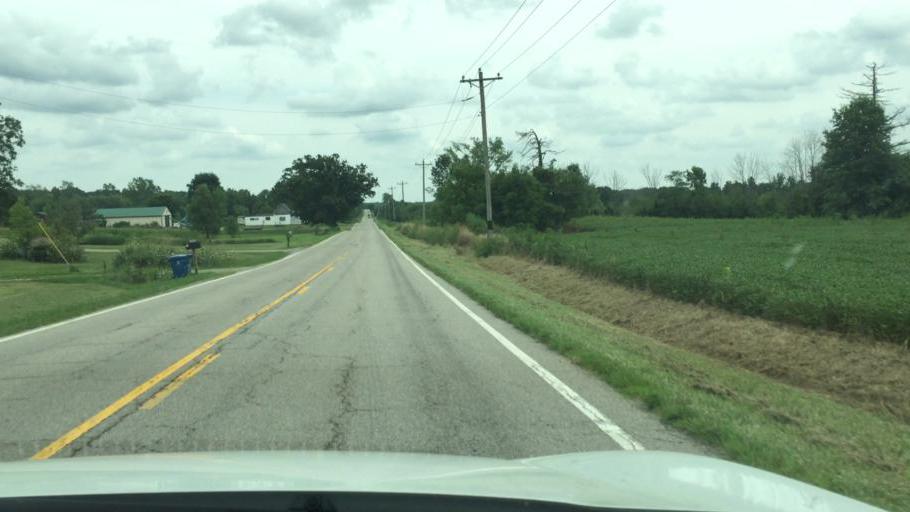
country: US
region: Ohio
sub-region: Champaign County
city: North Lewisburg
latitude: 40.2538
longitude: -83.4872
